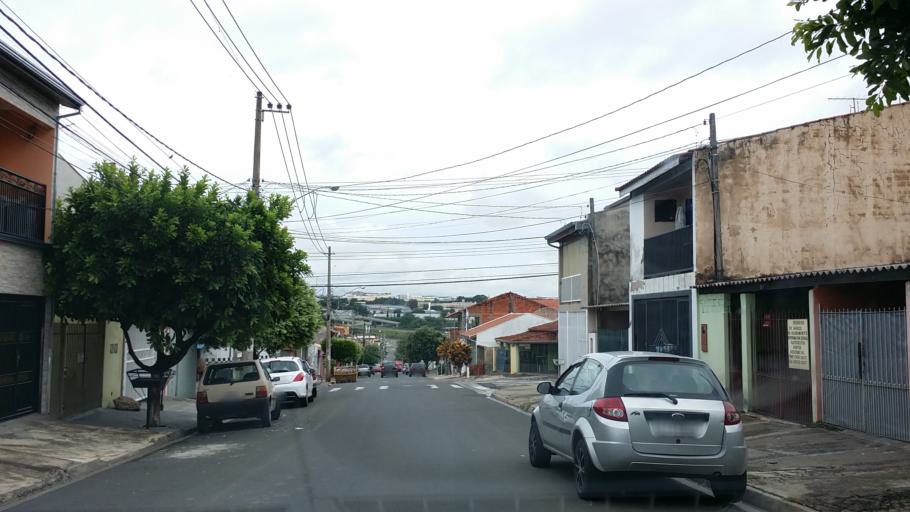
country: BR
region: Sao Paulo
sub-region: Indaiatuba
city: Indaiatuba
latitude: -23.1265
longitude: -47.2371
